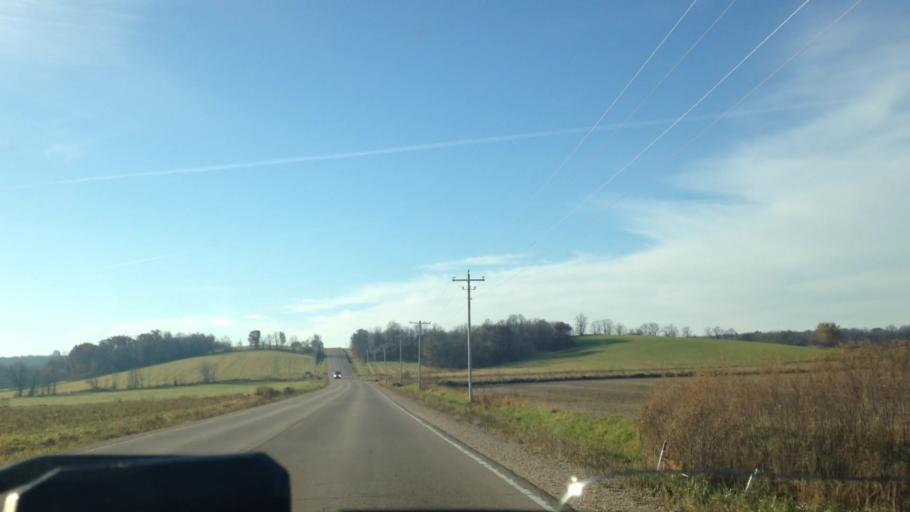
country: US
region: Wisconsin
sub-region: Dodge County
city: Mayville
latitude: 43.4660
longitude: -88.5000
